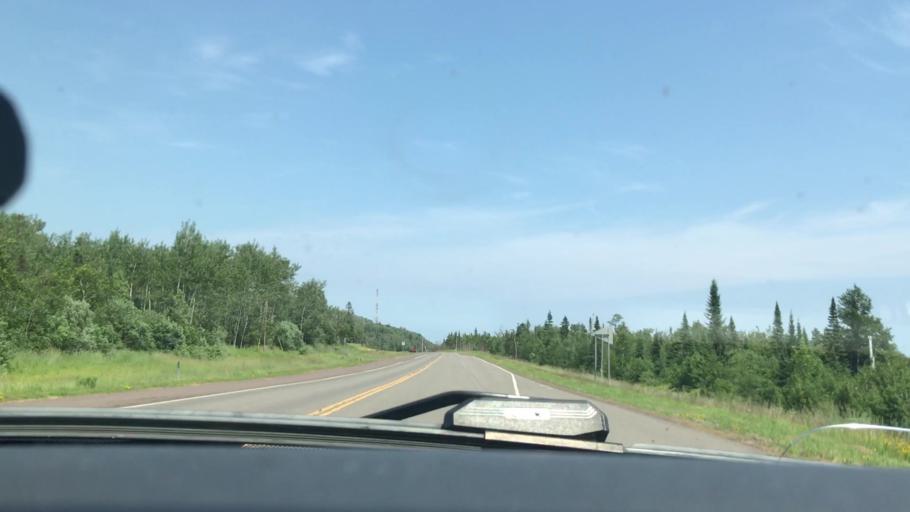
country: US
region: Minnesota
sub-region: Lake County
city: Silver Bay
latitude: 47.3132
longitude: -91.2313
